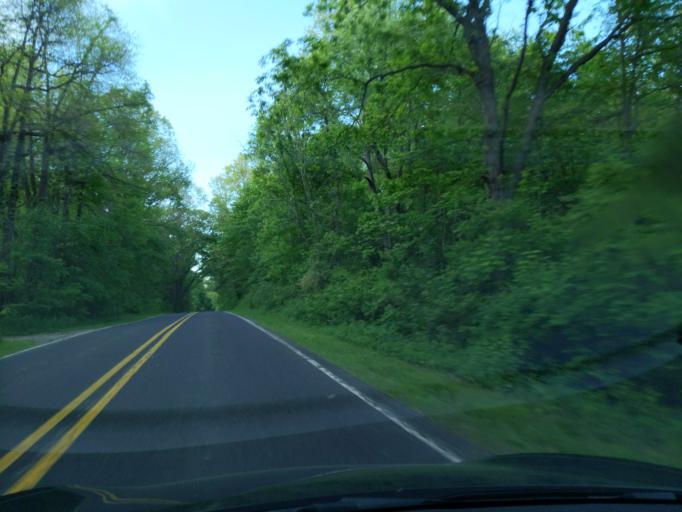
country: US
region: Michigan
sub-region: Ingham County
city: Stockbridge
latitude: 42.5179
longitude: -84.3052
